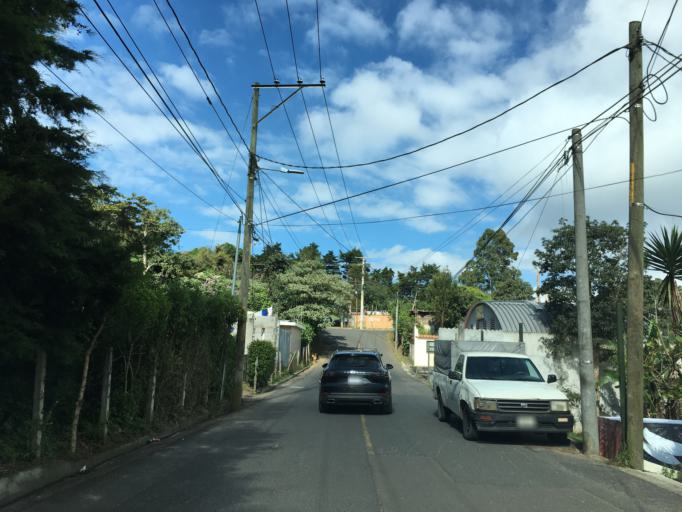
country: GT
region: Guatemala
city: San Jose Pinula
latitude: 14.5668
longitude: -90.4393
